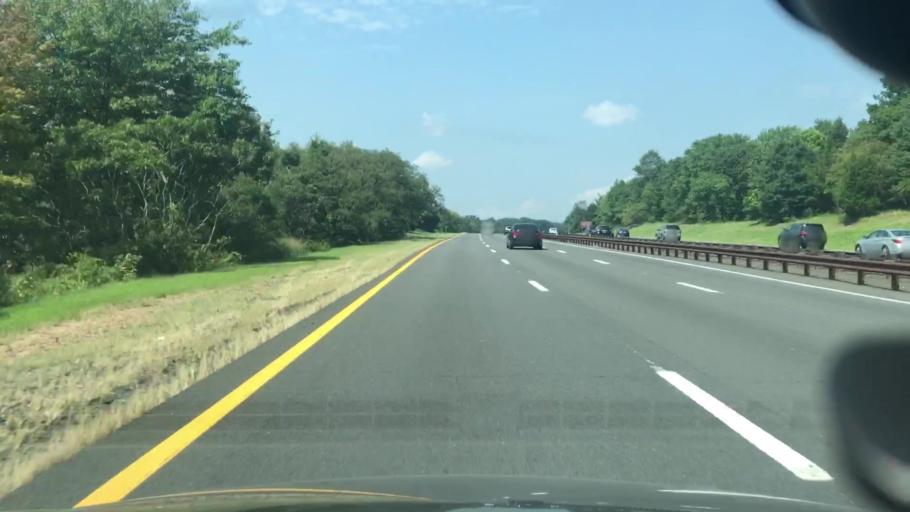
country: US
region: New Jersey
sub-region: Monmouth County
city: Matawan
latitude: 40.4291
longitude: -74.2361
